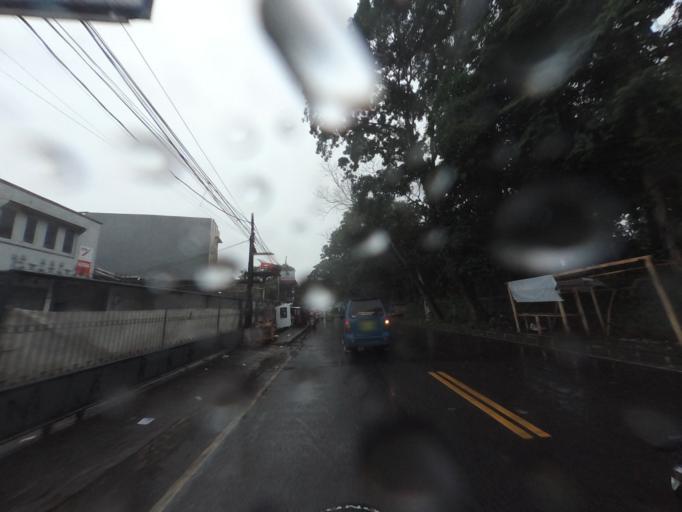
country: ID
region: West Java
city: Caringin
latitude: -6.6580
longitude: 106.8580
